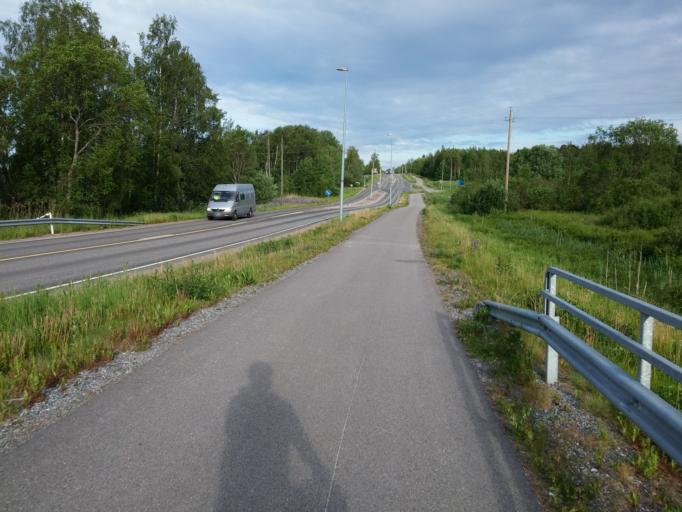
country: FI
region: Uusimaa
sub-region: Helsinki
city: Kirkkonummi
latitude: 60.1364
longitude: 24.5175
